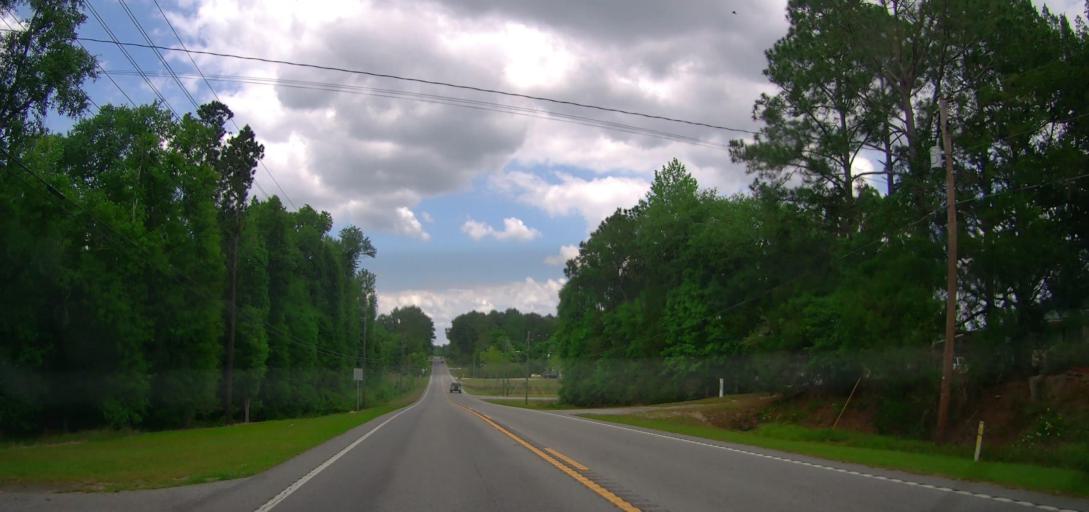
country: US
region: Georgia
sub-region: Treutlen County
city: Soperton
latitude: 32.3655
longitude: -82.5954
